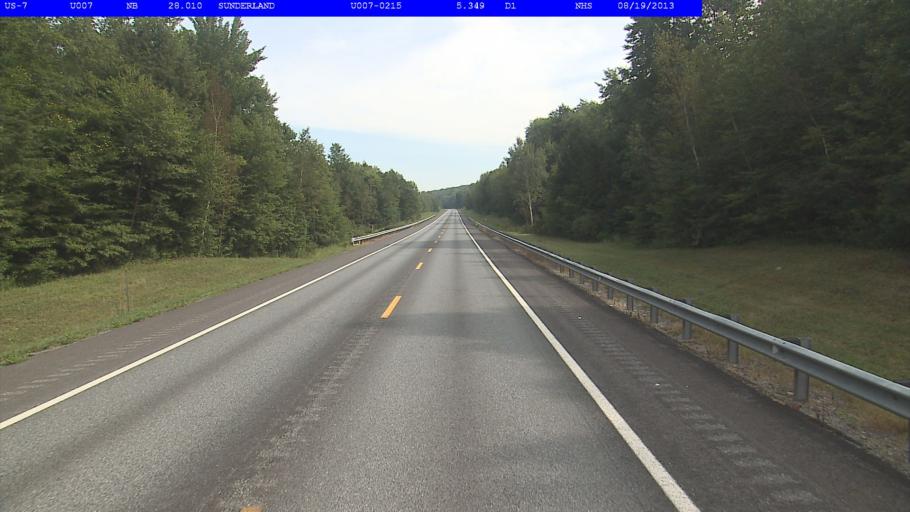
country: US
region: Vermont
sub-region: Bennington County
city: Arlington
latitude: 43.0955
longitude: -73.0982
